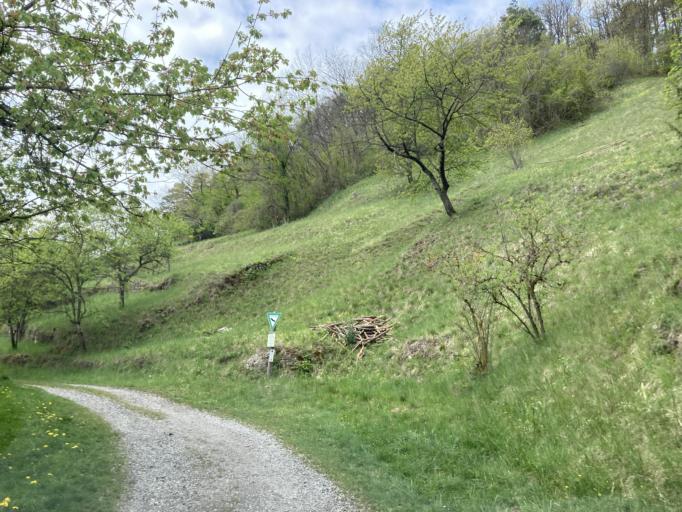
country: DE
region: Baden-Wuerttemberg
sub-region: Tuebingen Region
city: Tuebingen
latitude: 48.5063
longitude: 8.9951
